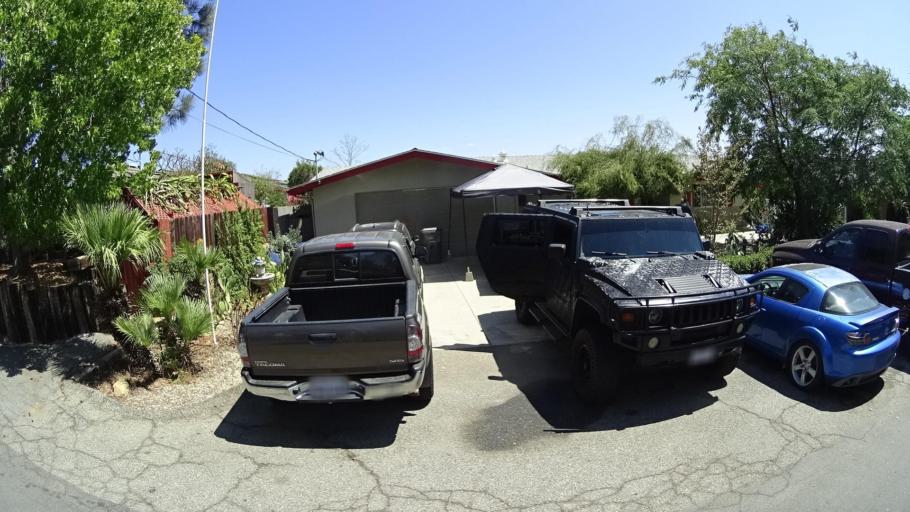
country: US
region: California
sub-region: San Diego County
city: Fallbrook
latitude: 33.3836
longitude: -117.2557
